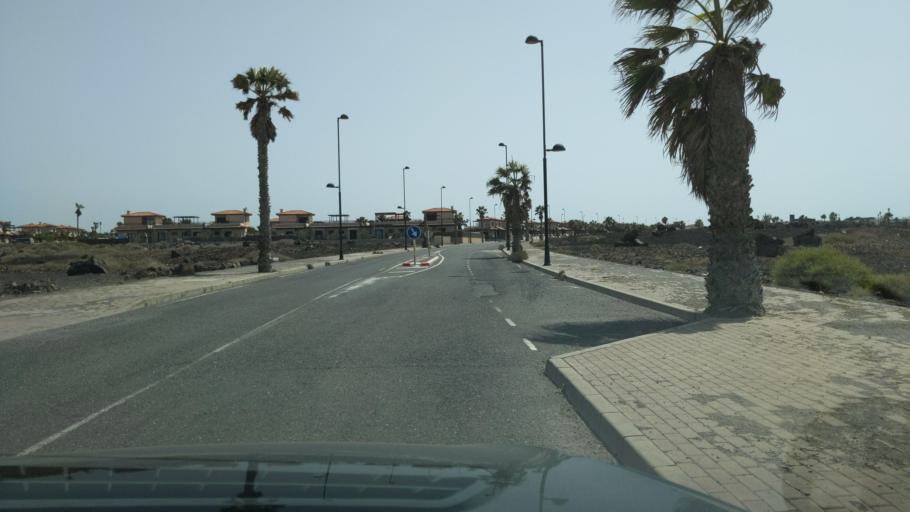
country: ES
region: Canary Islands
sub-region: Provincia de Las Palmas
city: Corralejo
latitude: 28.7336
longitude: -13.9456
